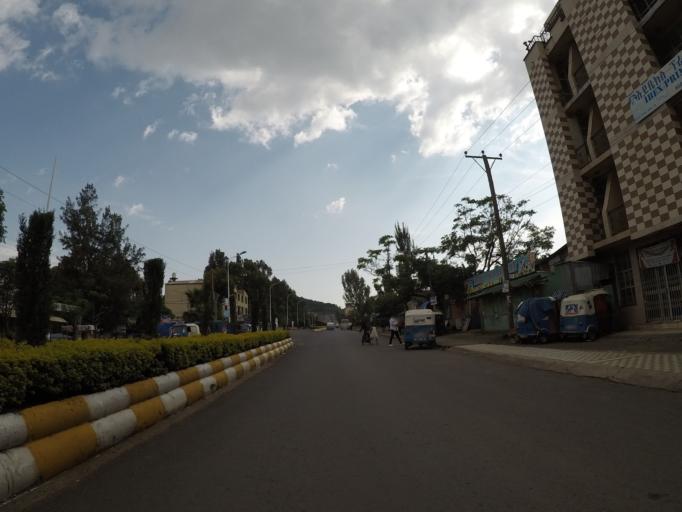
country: ET
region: Amhara
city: Gondar
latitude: 12.5971
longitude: 37.4497
